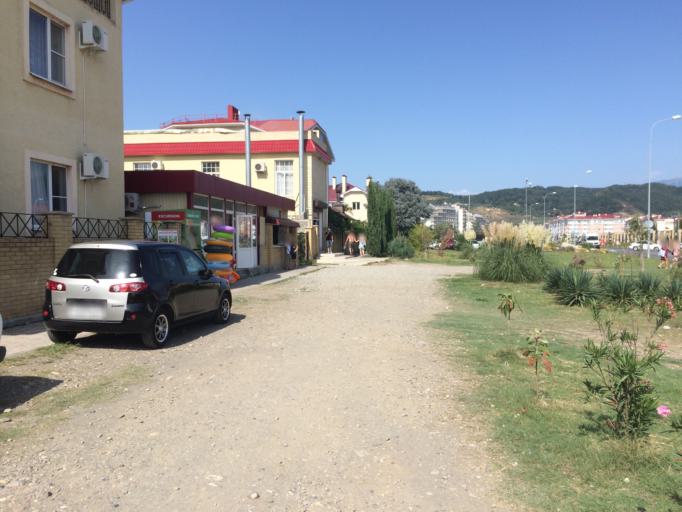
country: RU
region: Krasnodarskiy
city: Adler
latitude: 43.3970
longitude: 39.9741
